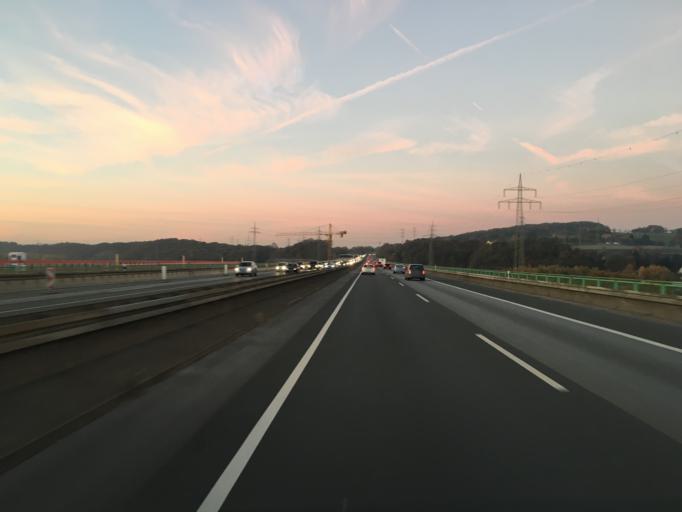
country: DE
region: North Rhine-Westphalia
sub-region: Regierungsbezirk Arnsberg
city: Hagen
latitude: 51.3806
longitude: 7.5248
